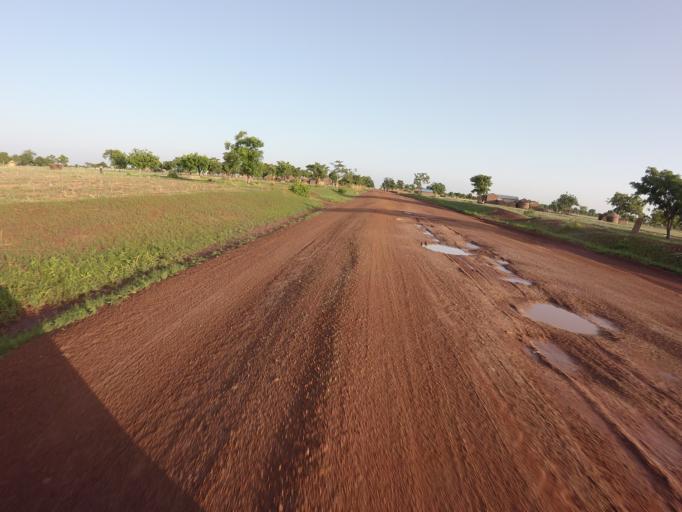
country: TG
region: Savanes
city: Sansanne-Mango
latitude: 10.2682
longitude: -0.0811
